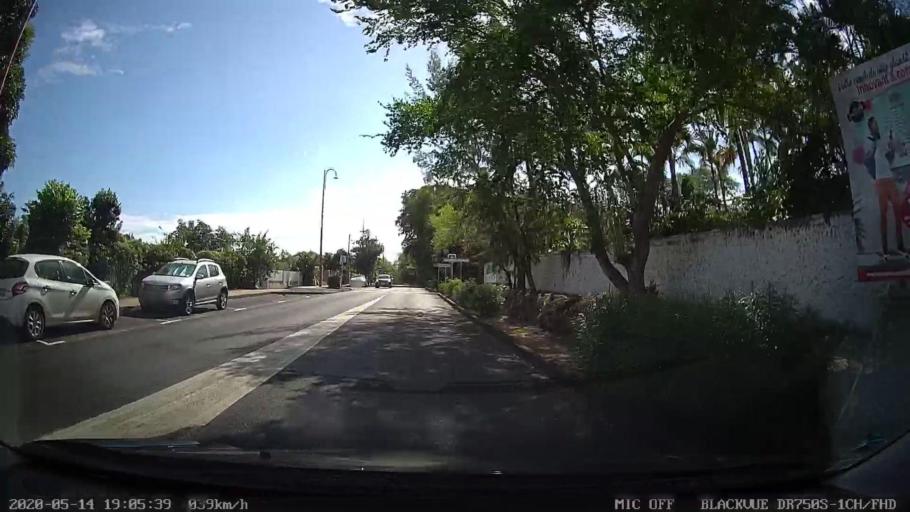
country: RE
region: Reunion
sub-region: Reunion
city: La Possession
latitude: -20.9358
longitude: 55.3334
